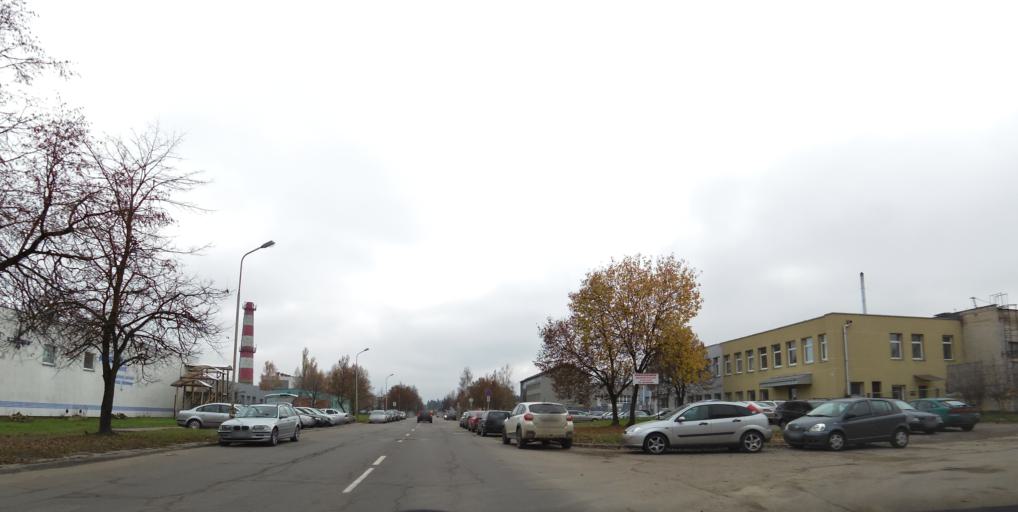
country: LT
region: Vilnius County
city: Vilkpede
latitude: 54.6363
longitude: 25.2665
